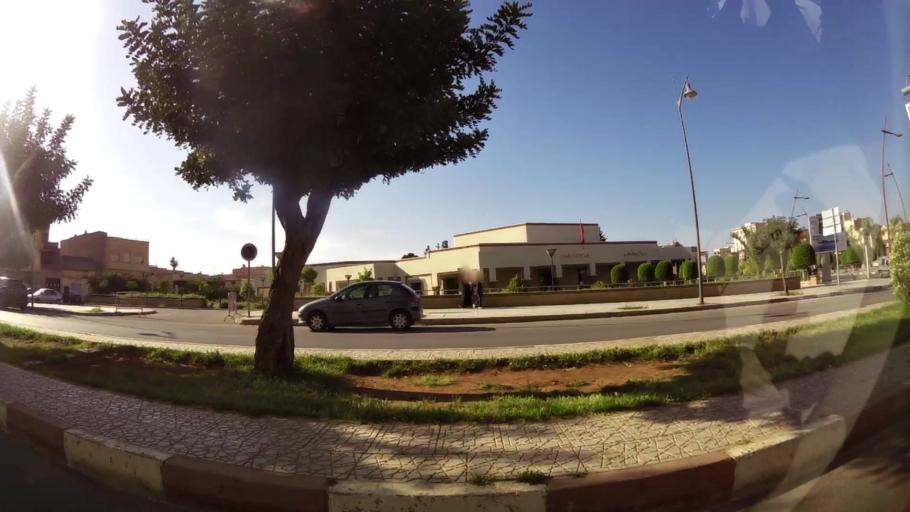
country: MA
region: Oriental
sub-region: Oujda-Angad
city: Oujda
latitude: 34.6898
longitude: -1.9192
